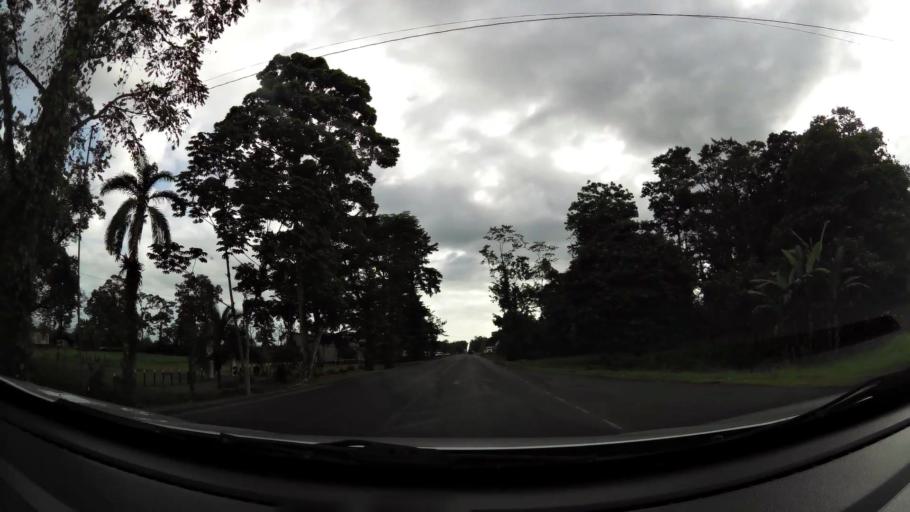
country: CR
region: Limon
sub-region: Canton de Pococi
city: Guapiles
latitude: 10.2035
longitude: -83.7712
